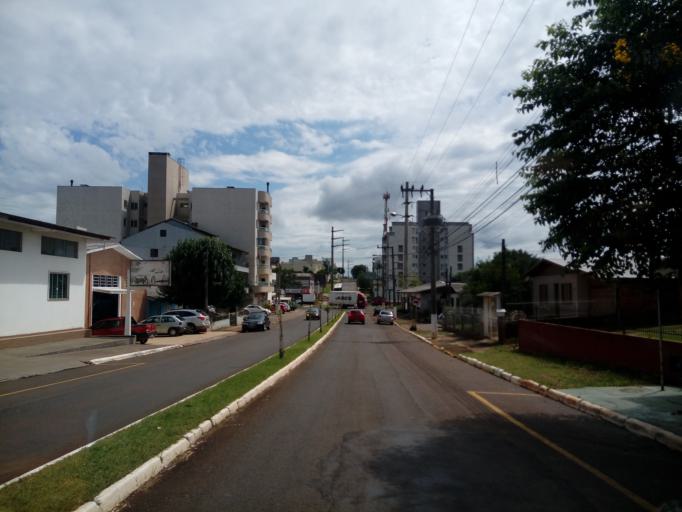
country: BR
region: Santa Catarina
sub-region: Chapeco
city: Chapeco
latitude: -27.1060
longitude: -52.5998
